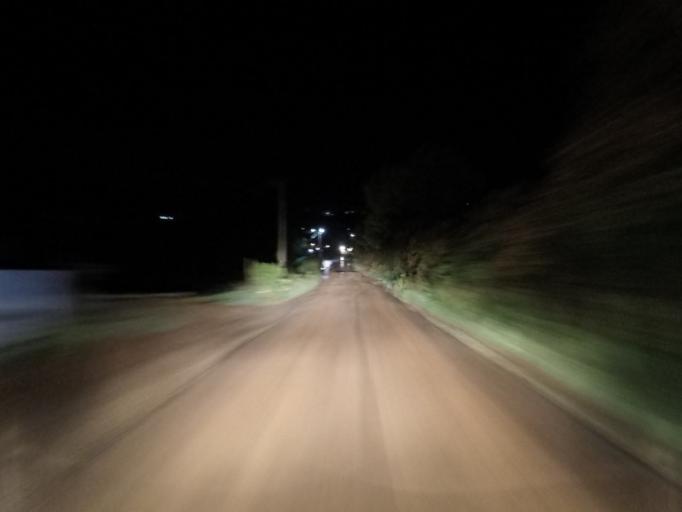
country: IN
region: Tamil Nadu
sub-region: Nilgiri
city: Kotagiri
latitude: 11.4810
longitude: 76.8219
